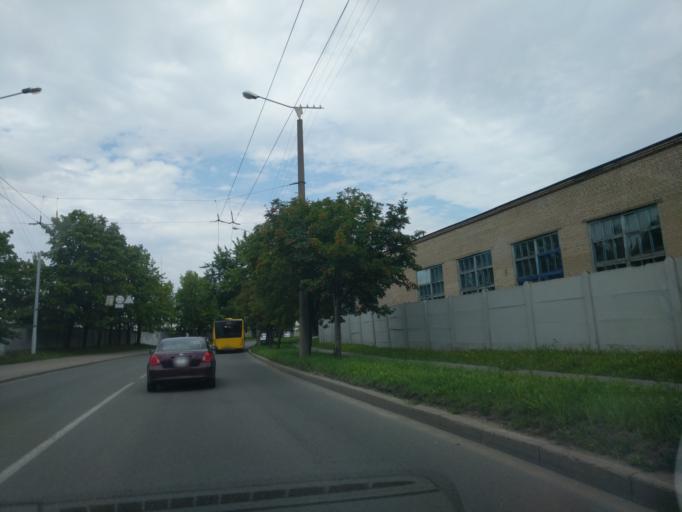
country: BY
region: Minsk
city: Novoye Medvezhino
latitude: 53.8881
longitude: 27.4804
